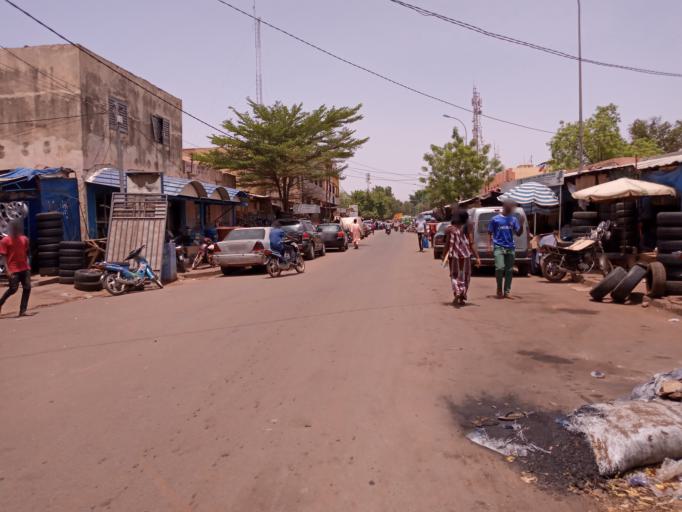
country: ML
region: Bamako
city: Bamako
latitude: 12.6413
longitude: -8.0008
